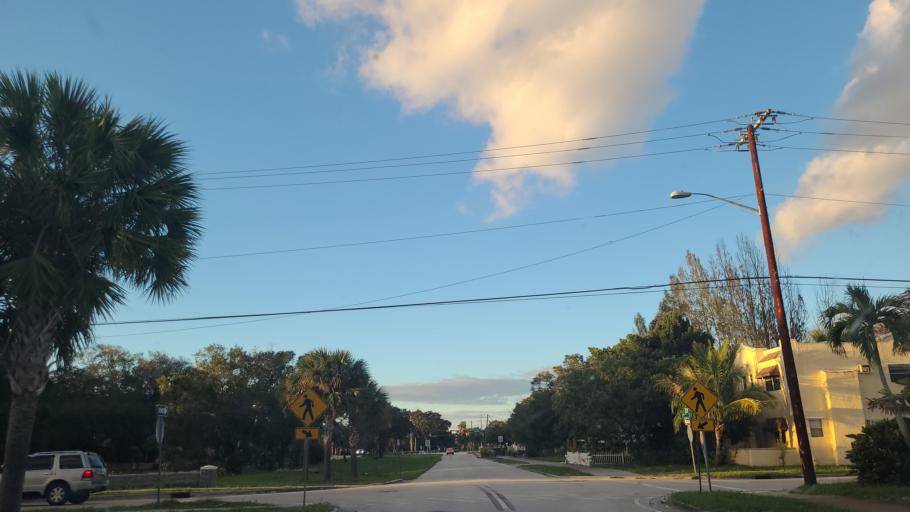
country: US
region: Florida
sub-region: Indian River County
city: Vero Beach
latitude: 27.6359
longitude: -80.4055
